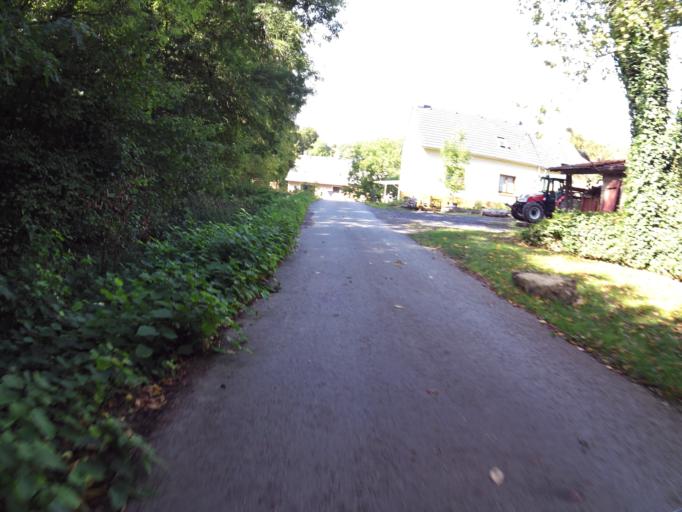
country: DE
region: Rheinland-Pfalz
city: Menningen
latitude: 49.8375
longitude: 6.4777
